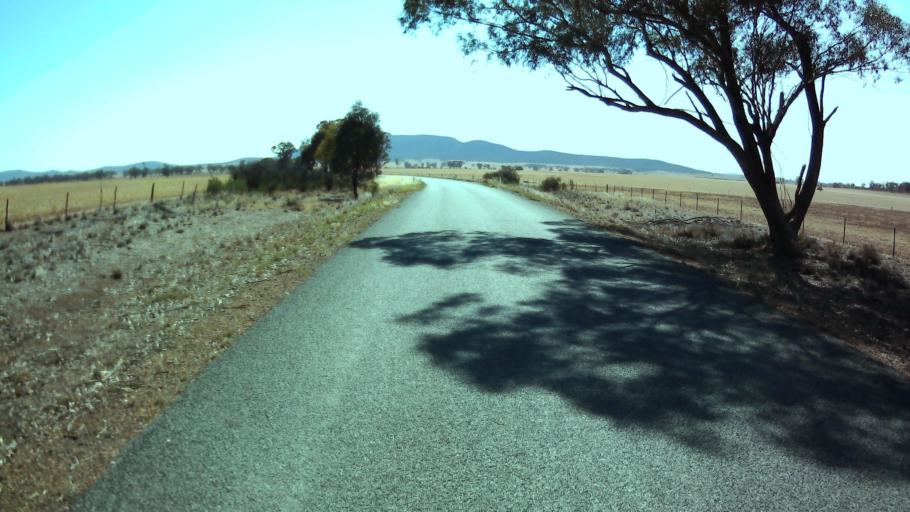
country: AU
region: New South Wales
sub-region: Weddin
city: Grenfell
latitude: -33.7531
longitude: 147.8635
